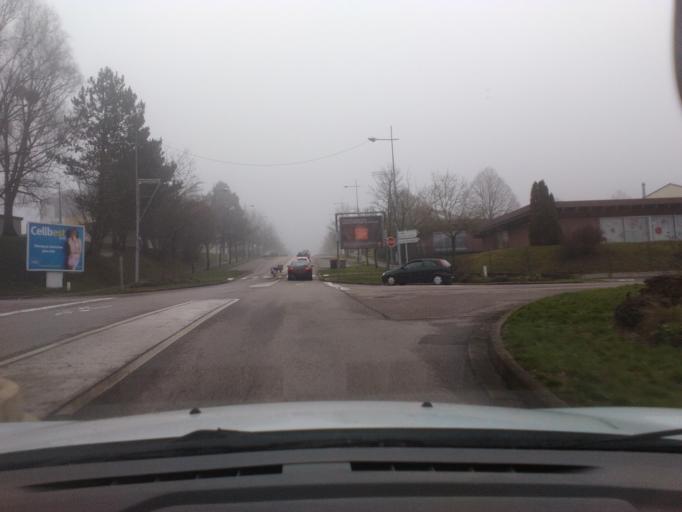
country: FR
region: Lorraine
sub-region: Departement des Vosges
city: Epinal
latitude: 48.1925
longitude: 6.4563
